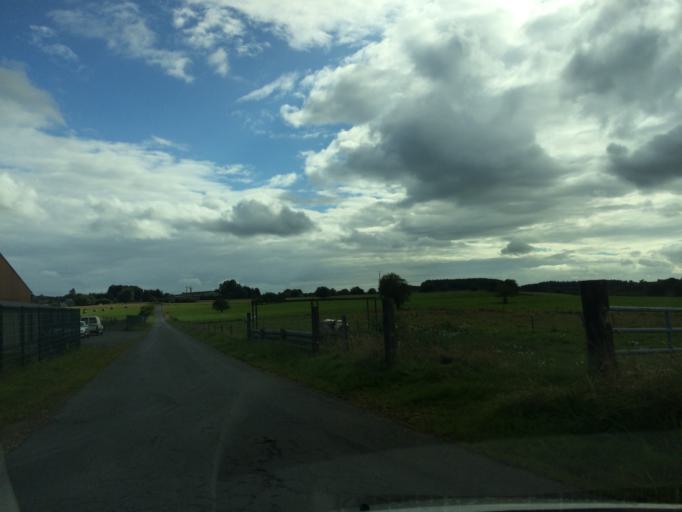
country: BE
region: Wallonia
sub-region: Province du Luxembourg
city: Chiny
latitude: 49.6946
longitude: 5.3621
